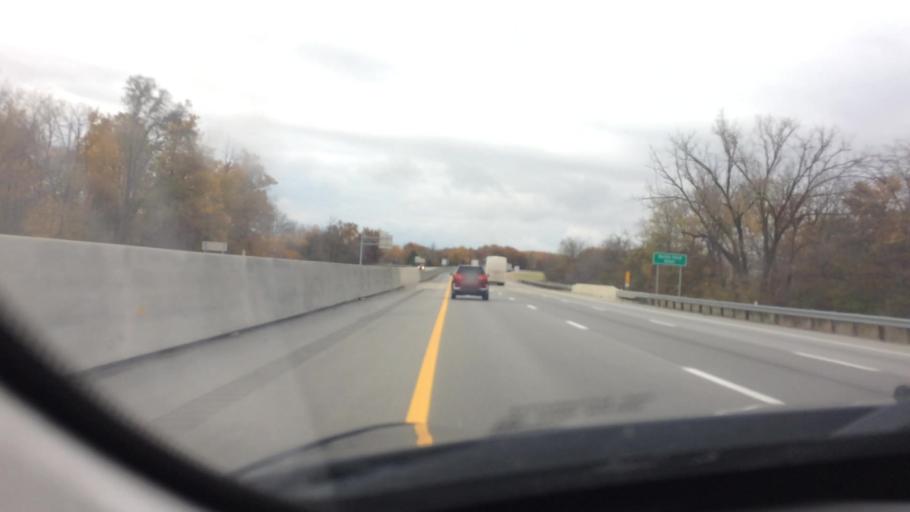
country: US
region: Ohio
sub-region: Wood County
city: North Baltimore
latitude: 41.1462
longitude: -83.6588
